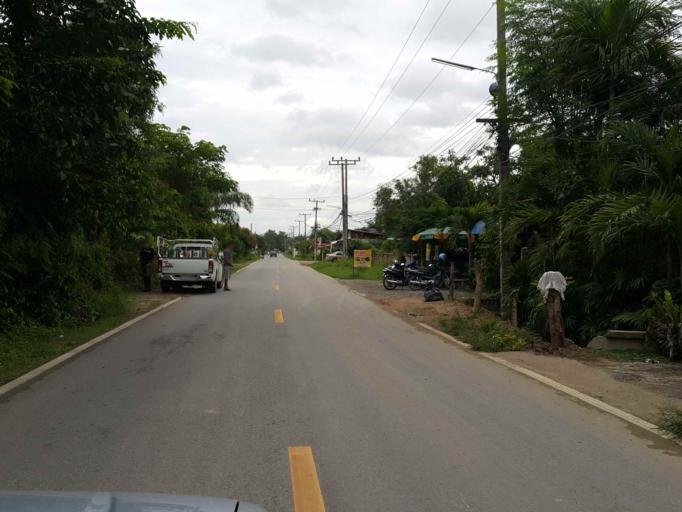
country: TH
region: Chiang Mai
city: San Sai
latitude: 18.8166
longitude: 99.0732
